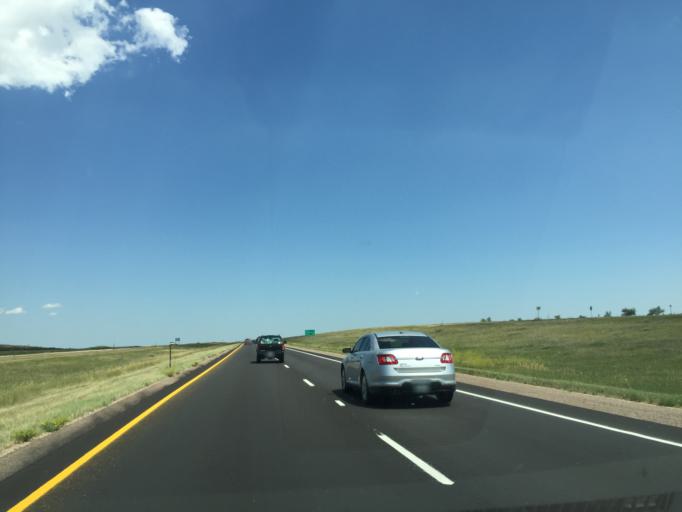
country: US
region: Colorado
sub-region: Lincoln County
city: Hugo
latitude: 39.2796
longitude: -103.3808
